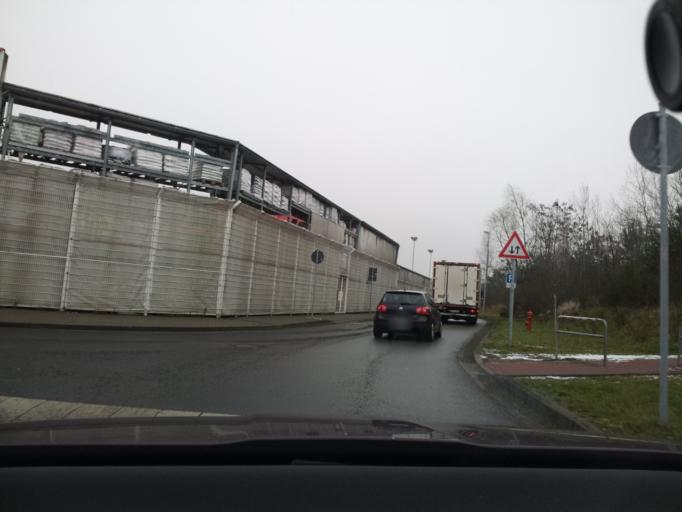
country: DE
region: Brandenburg
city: Wildau
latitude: 52.3126
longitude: 13.6125
